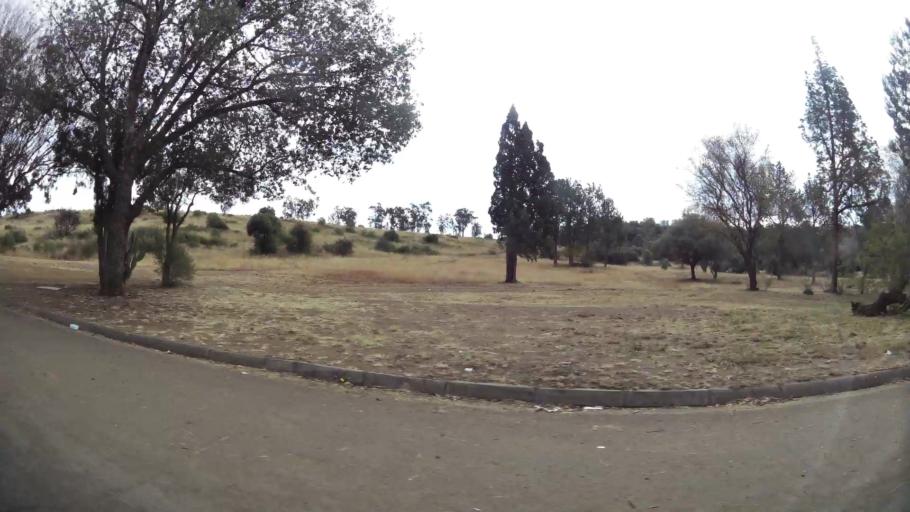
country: ZA
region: Orange Free State
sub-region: Mangaung Metropolitan Municipality
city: Bloemfontein
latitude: -29.1032
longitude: 26.2159
